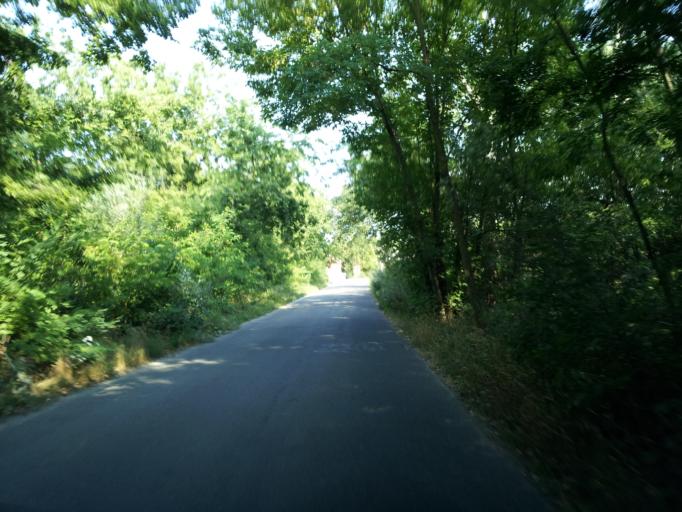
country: HU
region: Pest
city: Szigethalom
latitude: 47.3067
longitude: 19.0240
